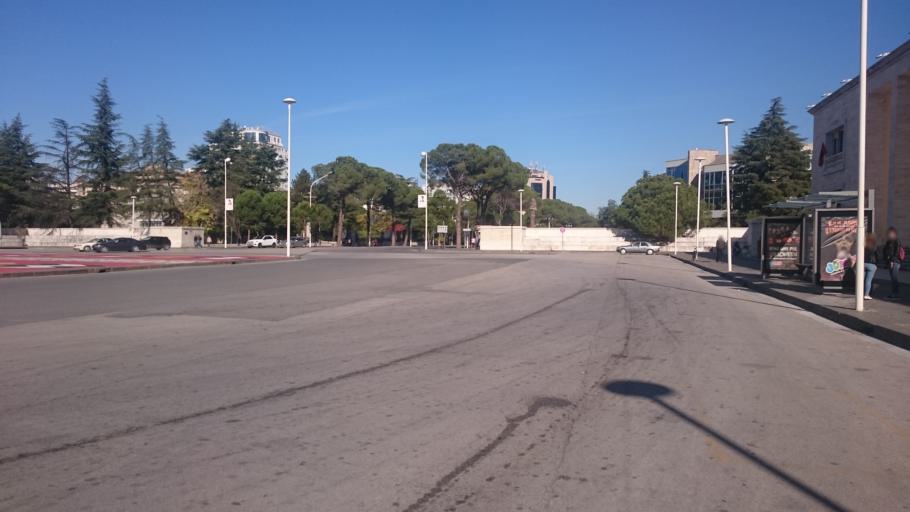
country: AL
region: Tirane
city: Tirana
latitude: 41.3178
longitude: 19.8218
